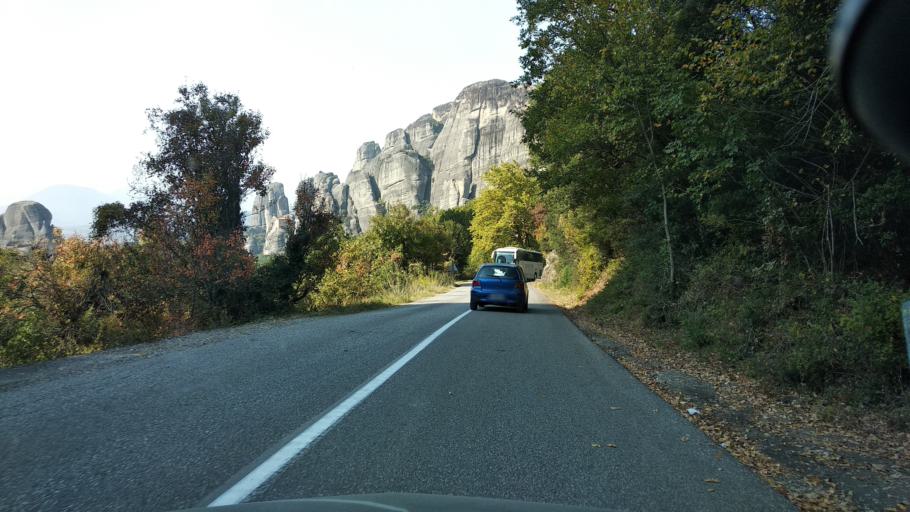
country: GR
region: Thessaly
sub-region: Trikala
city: Kastraki
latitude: 39.7187
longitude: 21.6334
